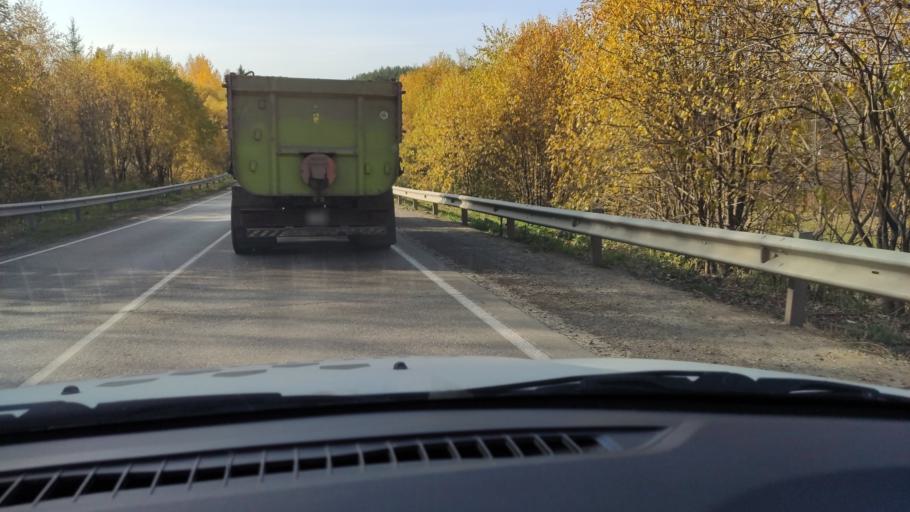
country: RU
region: Perm
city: Novyye Lyady
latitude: 58.0267
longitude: 56.6777
